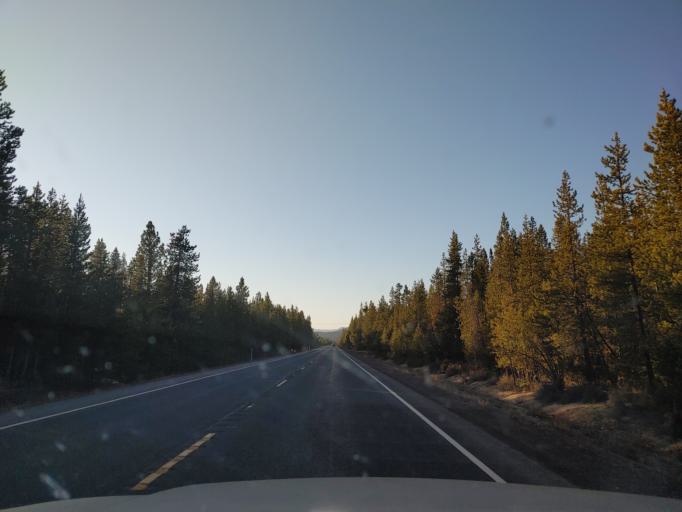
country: US
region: Oregon
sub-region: Deschutes County
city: La Pine
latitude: 43.3950
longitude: -121.8156
